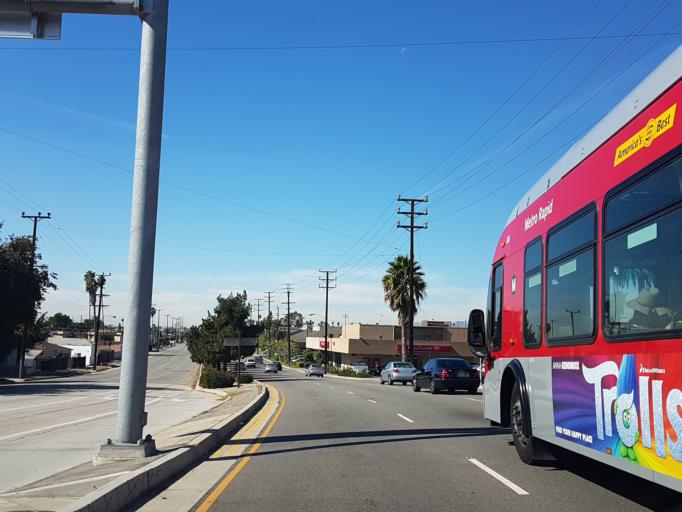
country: US
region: California
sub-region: Los Angeles County
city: West Hollywood
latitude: 34.0471
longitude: -118.3373
